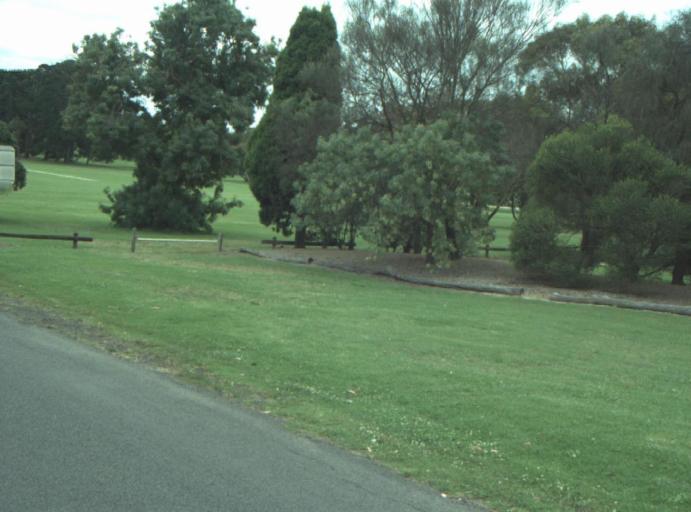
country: AU
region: Victoria
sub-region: Greater Geelong
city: East Geelong
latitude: -38.1546
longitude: 144.3801
